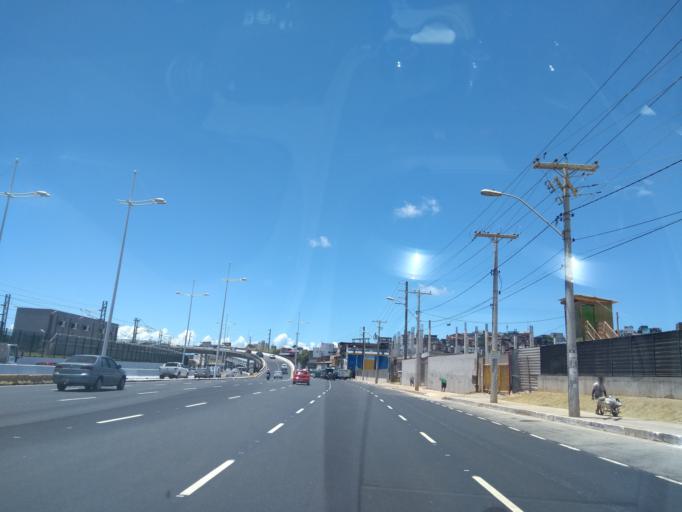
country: BR
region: Bahia
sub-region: Salvador
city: Salvador
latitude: -12.9752
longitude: -38.4581
